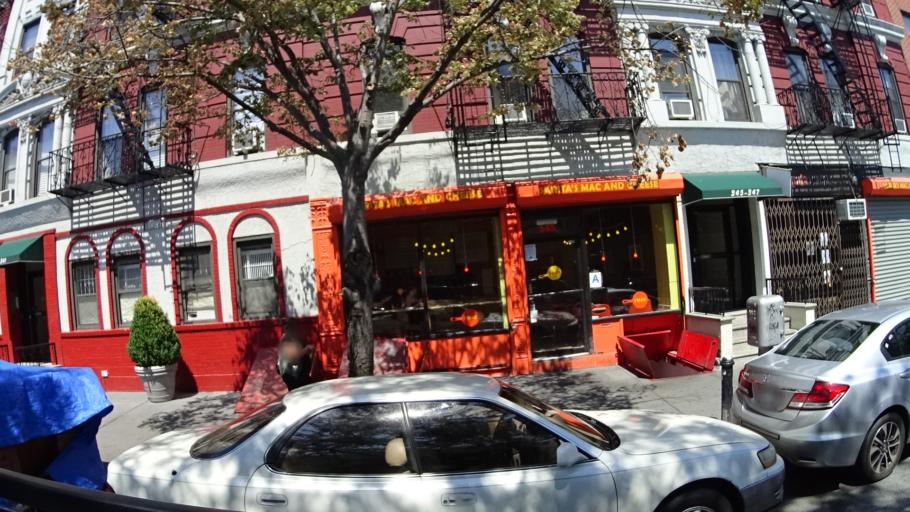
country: US
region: New York
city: New York City
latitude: 40.7303
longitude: -73.9841
